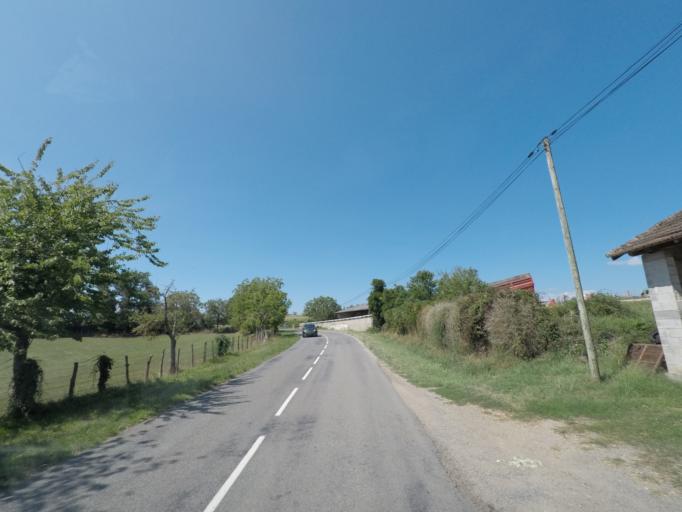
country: FR
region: Midi-Pyrenees
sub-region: Departement de l'Aveyron
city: Capdenac-Gare
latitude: 44.6188
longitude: 2.1097
